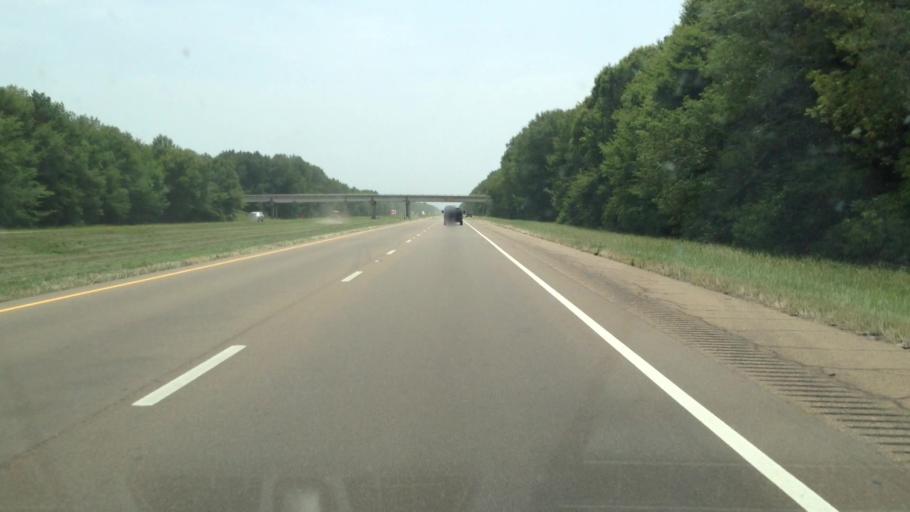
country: US
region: Texas
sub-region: Morris County
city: Naples
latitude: 33.3372
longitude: -94.6667
